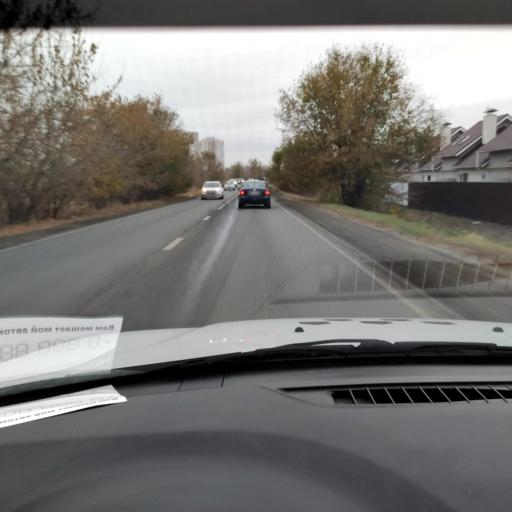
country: RU
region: Samara
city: Tol'yatti
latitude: 53.5145
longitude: 49.2425
